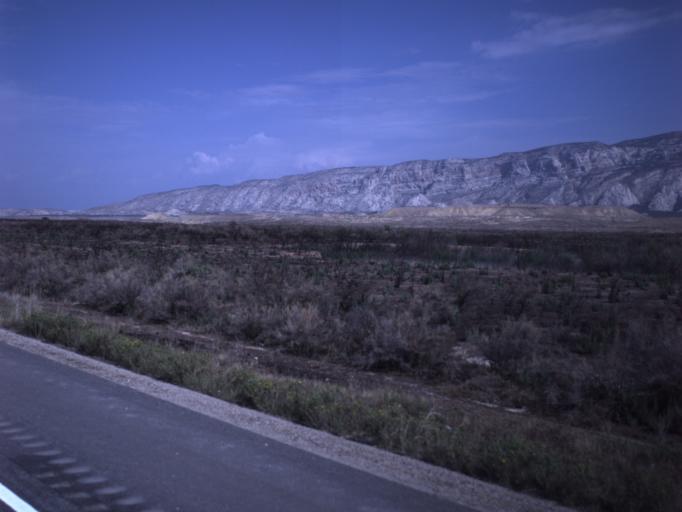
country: US
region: Utah
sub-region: Uintah County
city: Naples
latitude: 40.2882
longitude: -109.1494
